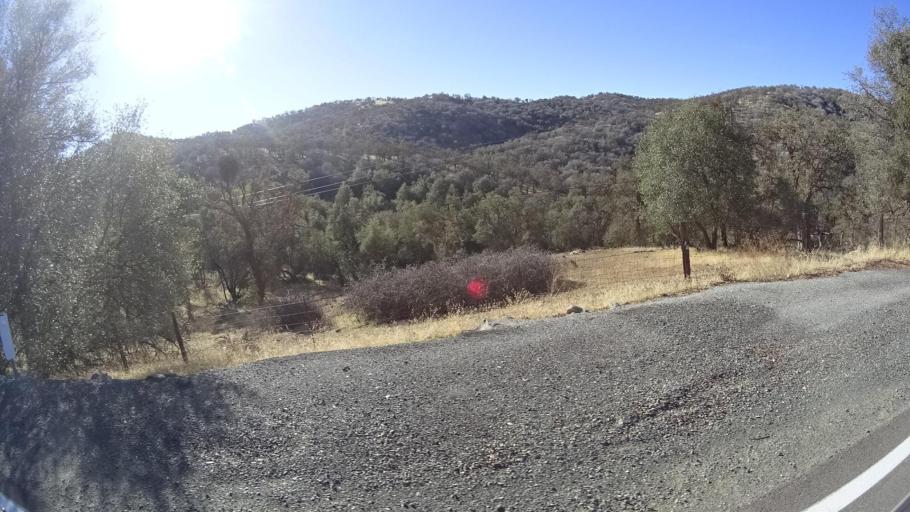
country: US
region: California
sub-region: Kern County
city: Alta Sierra
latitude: 35.7061
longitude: -118.7682
